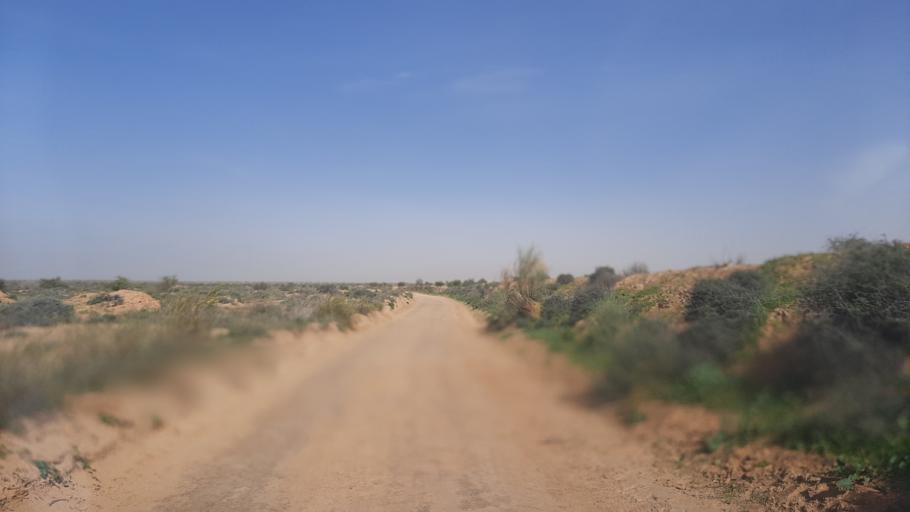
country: TN
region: Madanin
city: Zarzis
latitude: 33.4408
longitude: 10.8072
